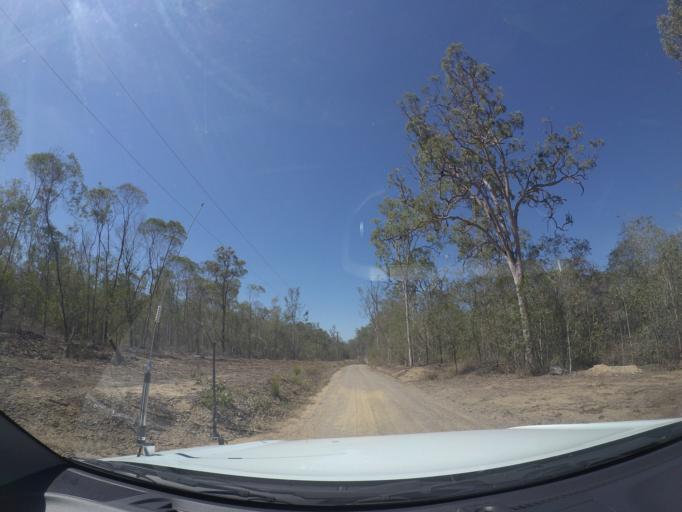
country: AU
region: Queensland
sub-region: Logan
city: North Maclean
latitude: -27.7671
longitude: 152.9379
